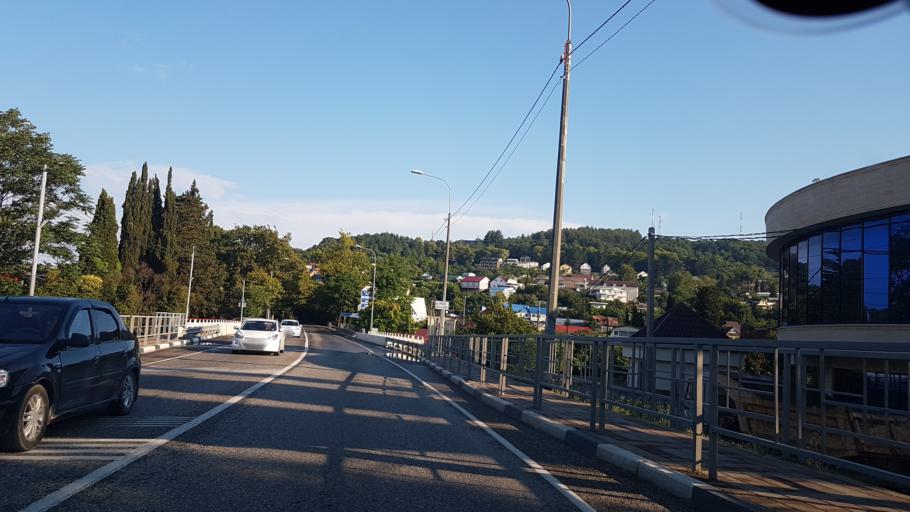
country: RU
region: Krasnodarskiy
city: Gornoye Loo
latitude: 43.7025
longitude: 39.5858
